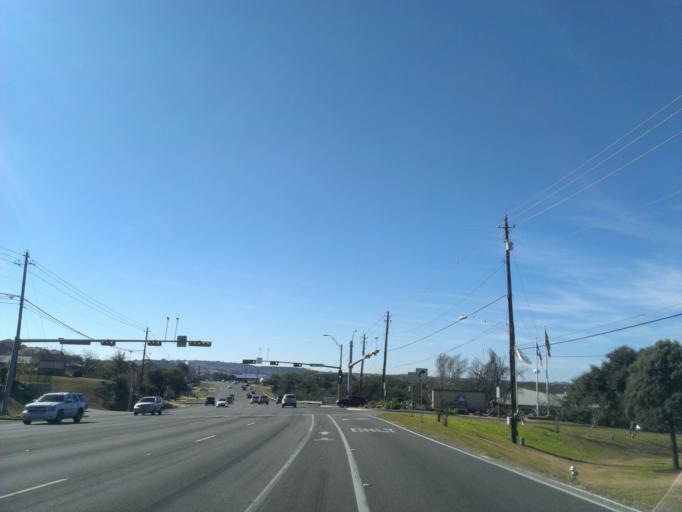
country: US
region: Texas
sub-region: Travis County
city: Lakeway
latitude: 30.3547
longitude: -97.9611
